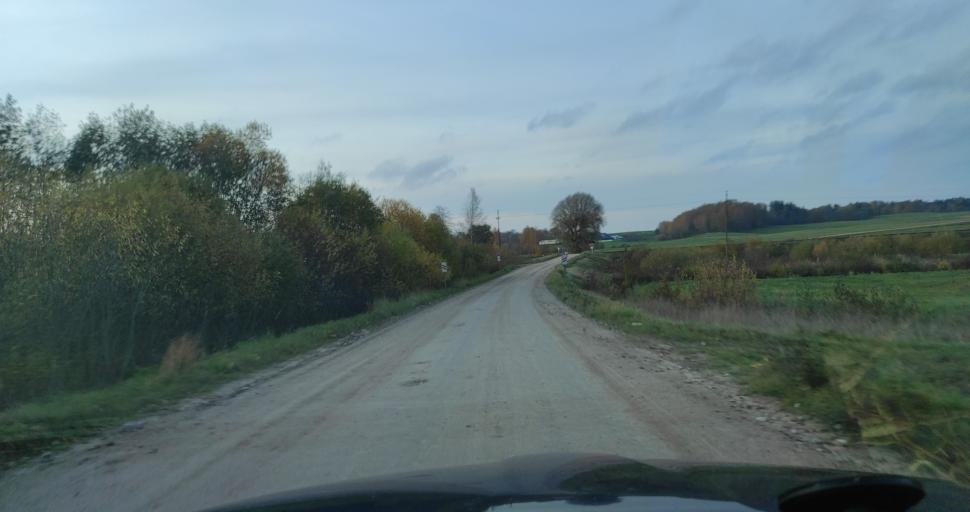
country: LV
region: Aizpute
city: Aizpute
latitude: 56.6470
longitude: 21.7973
